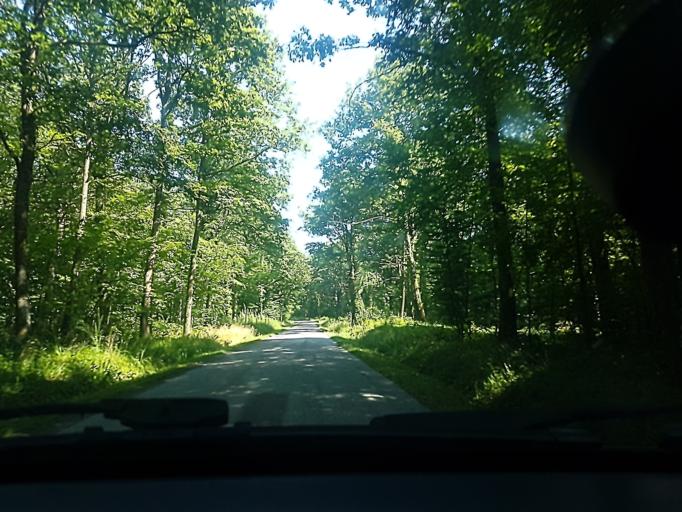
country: FR
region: Bourgogne
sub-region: Departement de Saone-et-Loire
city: Demigny
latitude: 46.8813
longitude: 4.8234
